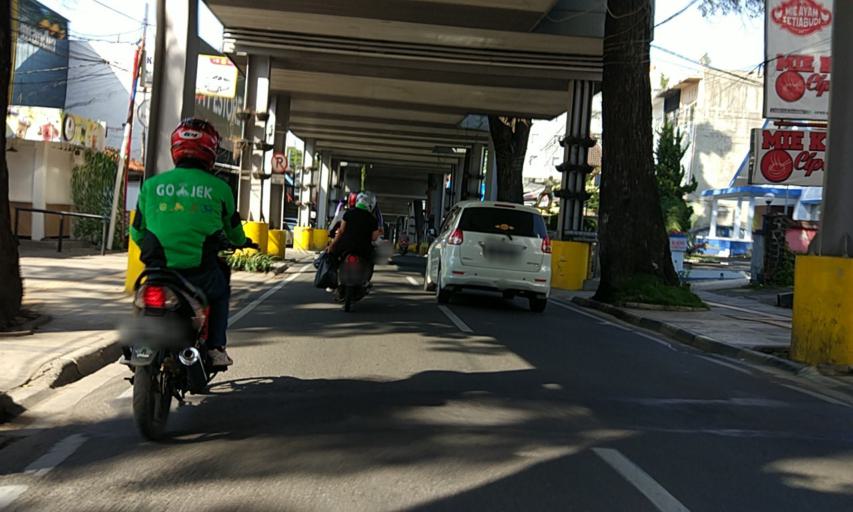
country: ID
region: West Java
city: Bandung
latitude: -6.8933
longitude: 107.6042
